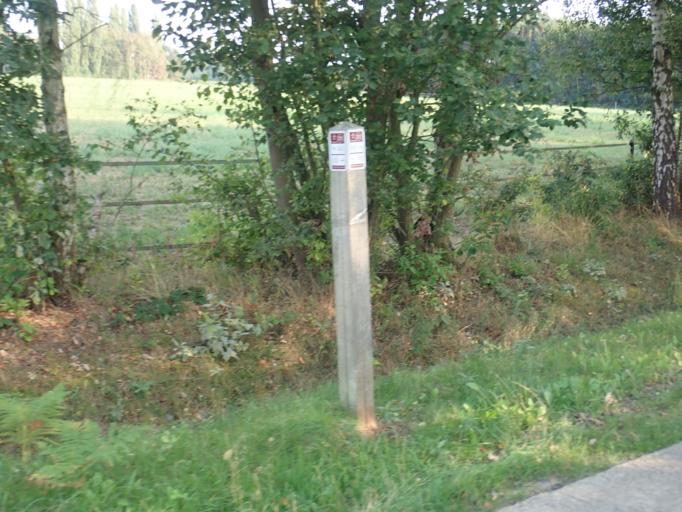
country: BE
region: Flanders
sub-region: Provincie Antwerpen
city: Nijlen
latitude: 51.1469
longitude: 4.6624
